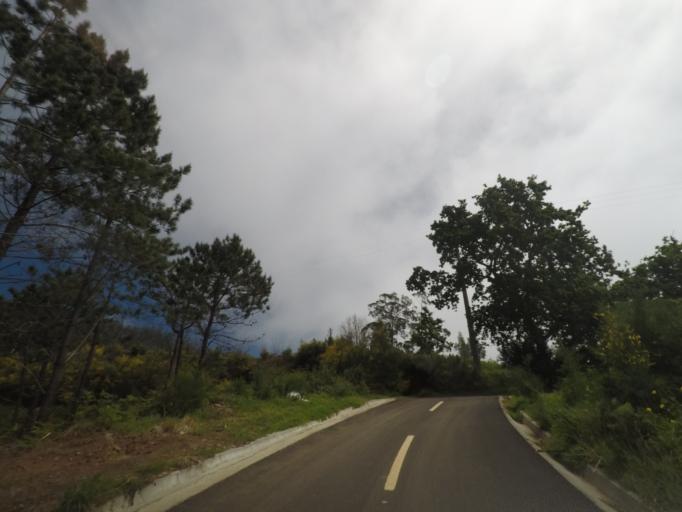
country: PT
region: Madeira
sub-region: Calheta
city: Arco da Calheta
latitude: 32.7227
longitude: -17.1197
